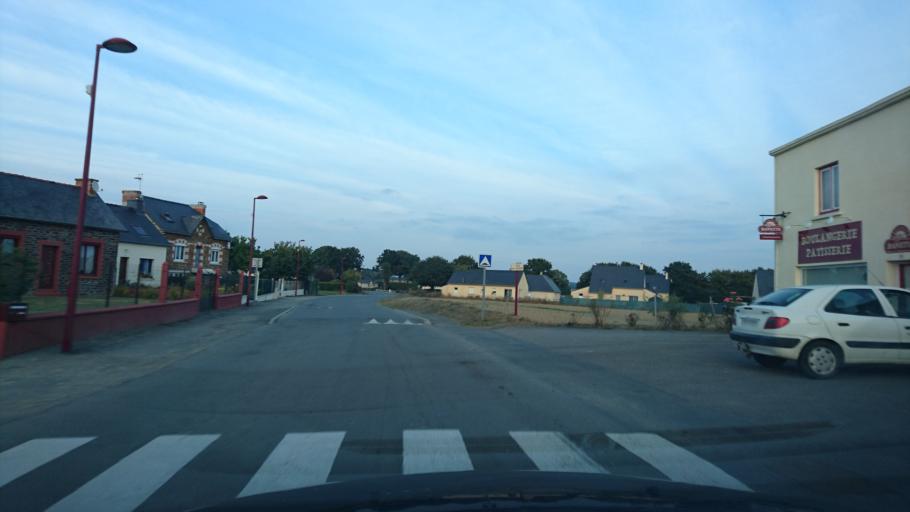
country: FR
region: Brittany
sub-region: Departement du Morbihan
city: Guer
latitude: 47.8764
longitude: -2.0812
